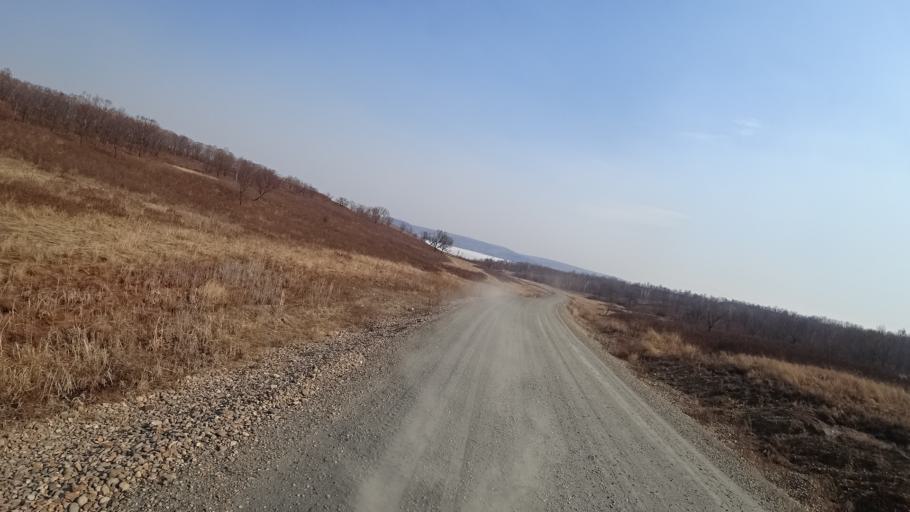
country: RU
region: Amur
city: Novobureyskiy
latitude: 49.8254
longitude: 129.9950
